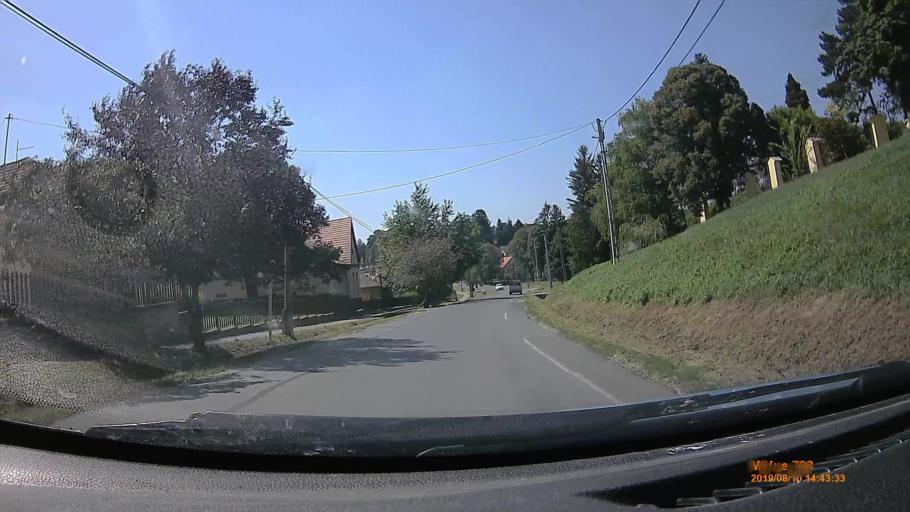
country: HU
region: Somogy
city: Somogyvar
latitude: 46.5796
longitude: 17.6538
